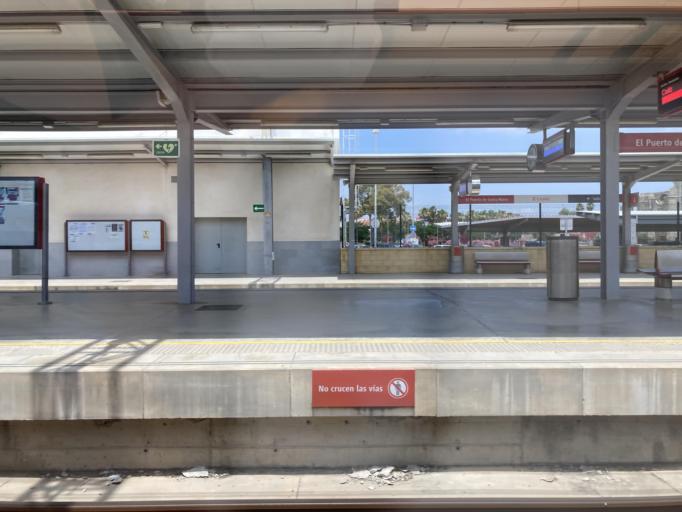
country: ES
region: Andalusia
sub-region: Provincia de Cadiz
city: El Puerto de Santa Maria
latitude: 36.6040
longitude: -6.2174
